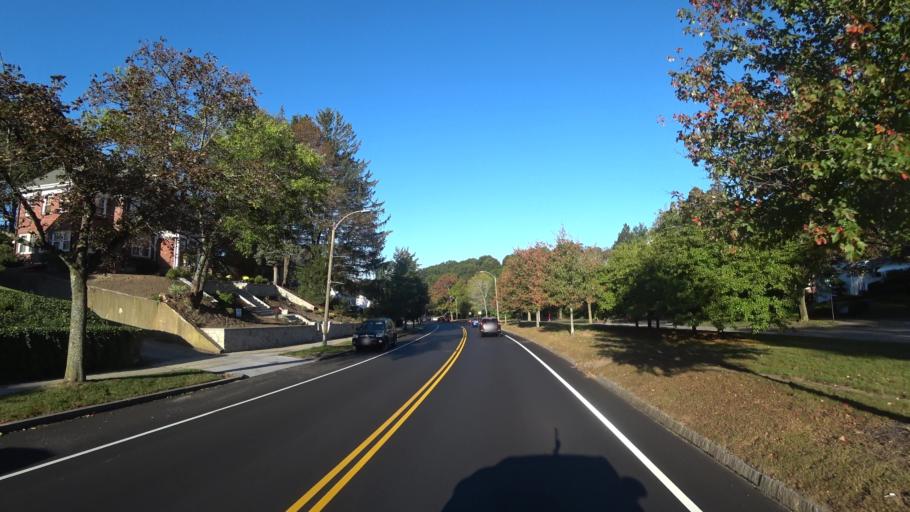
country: US
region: Massachusetts
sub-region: Middlesex County
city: Newton
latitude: 42.3385
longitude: -71.2048
